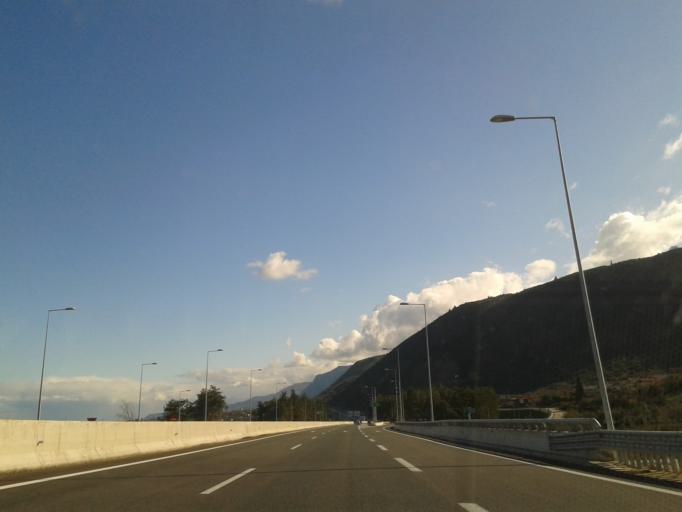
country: GR
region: West Greece
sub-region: Nomos Achaias
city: Temeni
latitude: 38.2227
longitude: 22.0999
